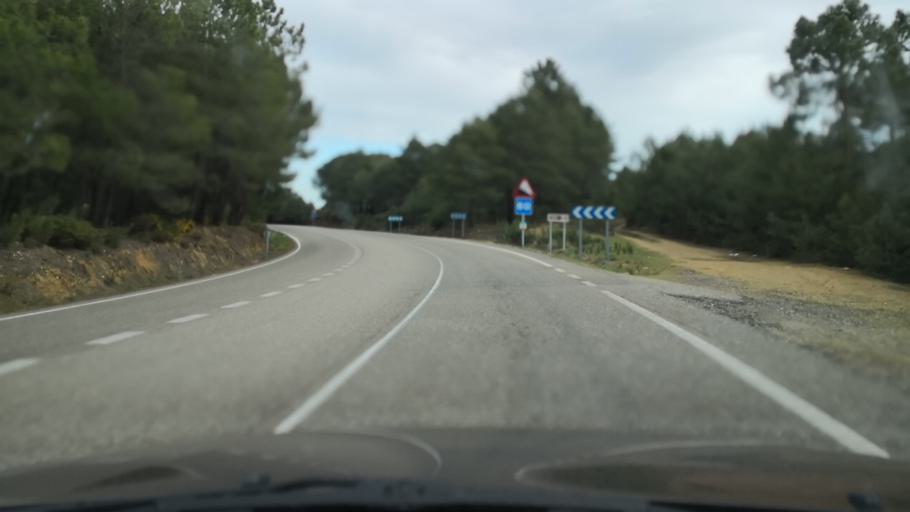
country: ES
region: Extremadura
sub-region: Provincia de Caceres
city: Acebo
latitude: 40.2053
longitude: -6.6736
